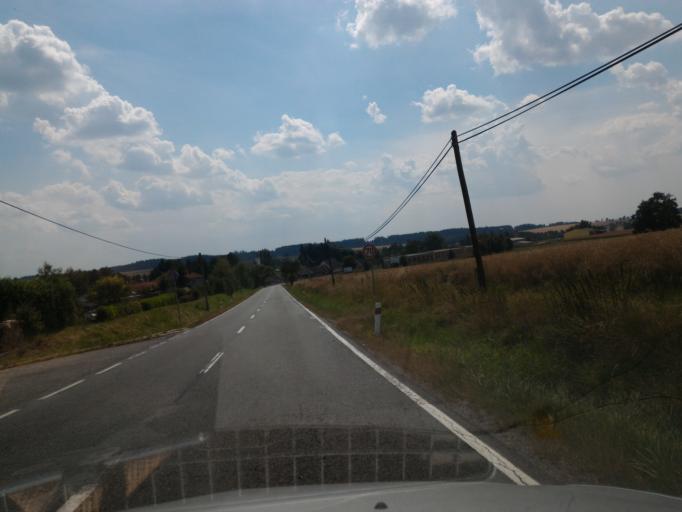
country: CZ
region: Vysocina
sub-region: Okres Jihlava
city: Polna
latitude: 49.4479
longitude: 15.7775
